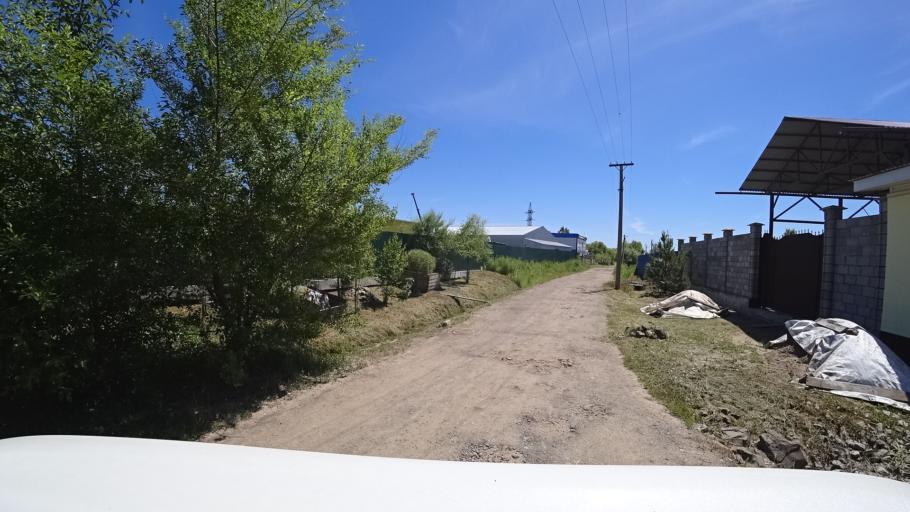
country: RU
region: Khabarovsk Krai
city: Topolevo
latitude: 48.5008
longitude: 135.1820
